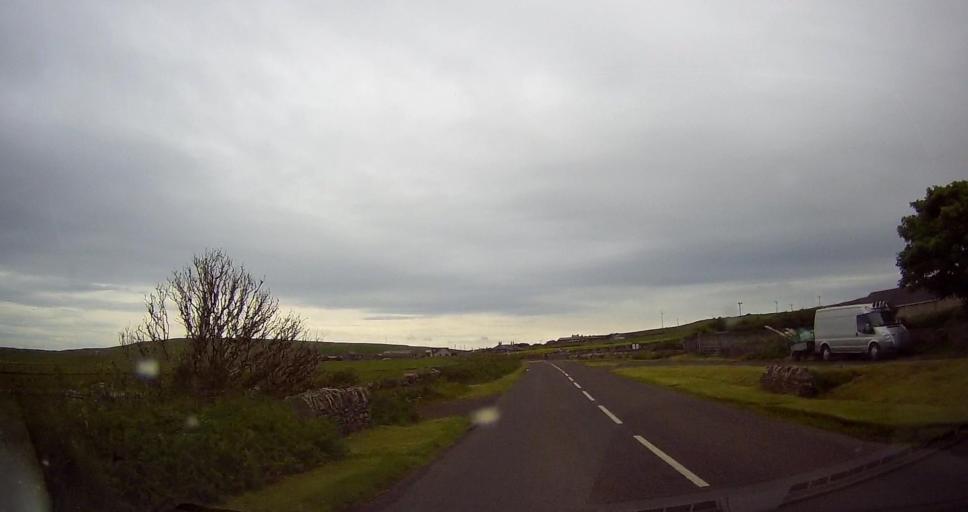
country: GB
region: Scotland
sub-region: Orkney Islands
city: Orkney
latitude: 59.1129
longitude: -3.1051
